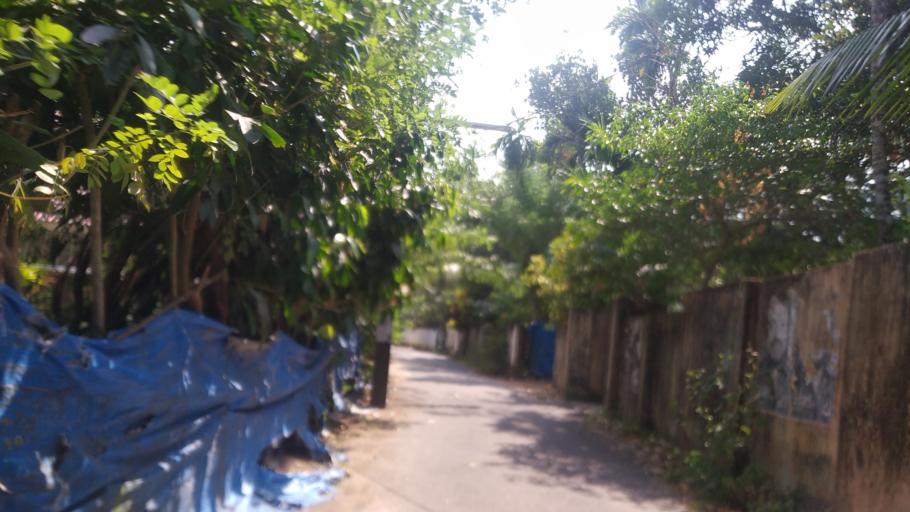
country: IN
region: Kerala
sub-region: Ernakulam
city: Elur
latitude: 10.1243
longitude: 76.2339
